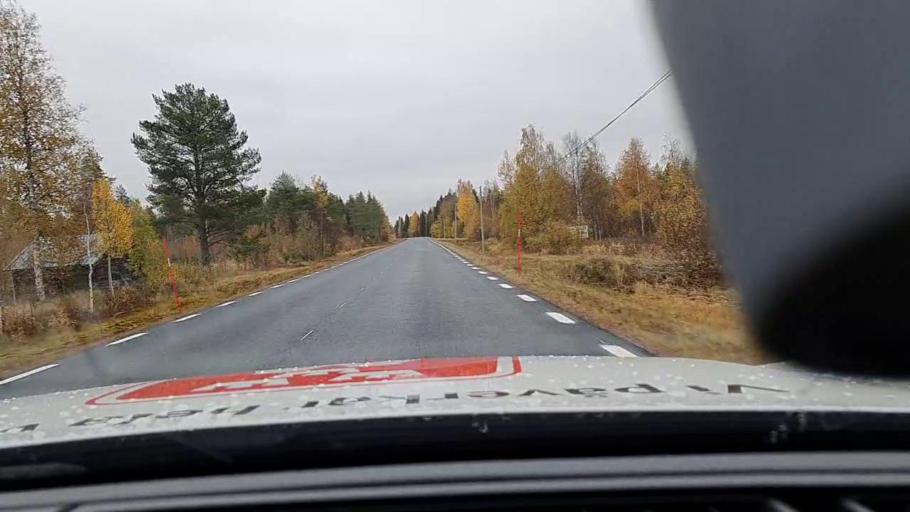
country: FI
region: Lapland
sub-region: Torniolaakso
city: Ylitornio
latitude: 66.1522
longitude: 23.8779
